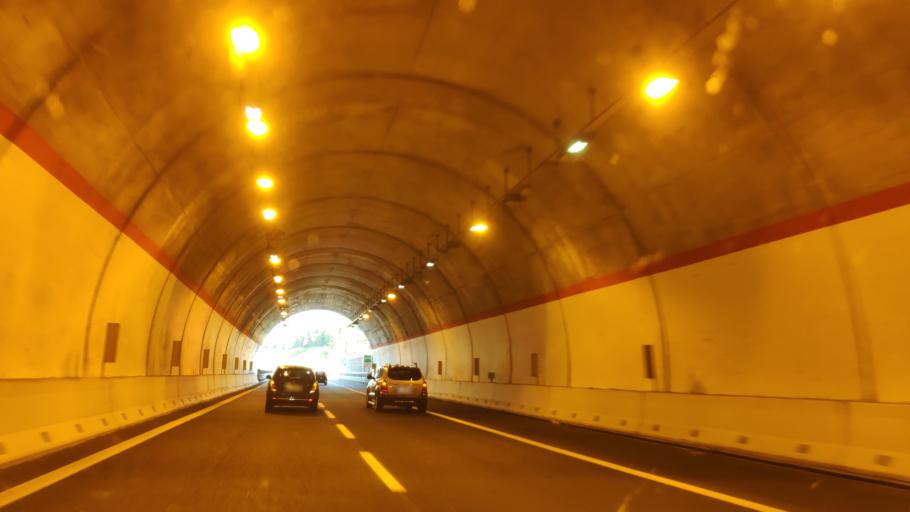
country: IT
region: Basilicate
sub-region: Provincia di Potenza
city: Lagonegro
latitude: 40.1264
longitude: 15.7775
